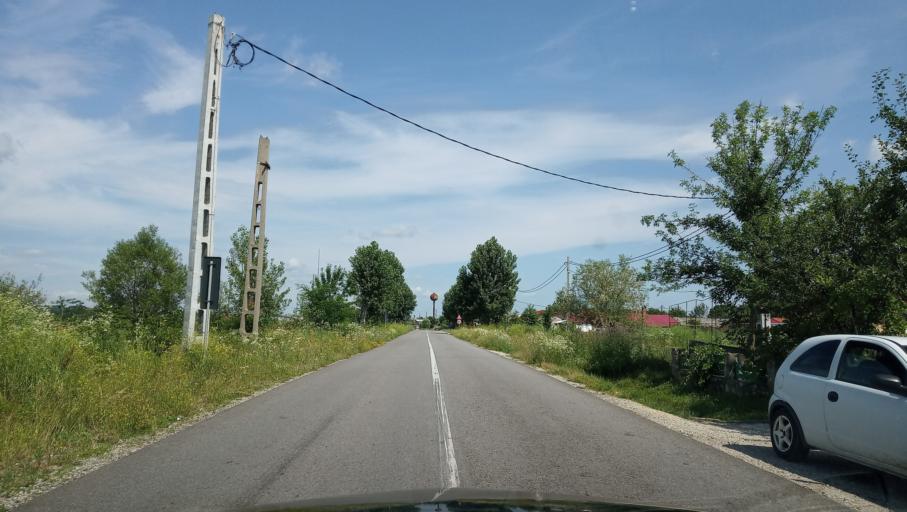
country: RO
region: Gorj
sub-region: Comuna Turcinesti
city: Turcinesti
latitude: 45.1317
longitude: 23.3678
